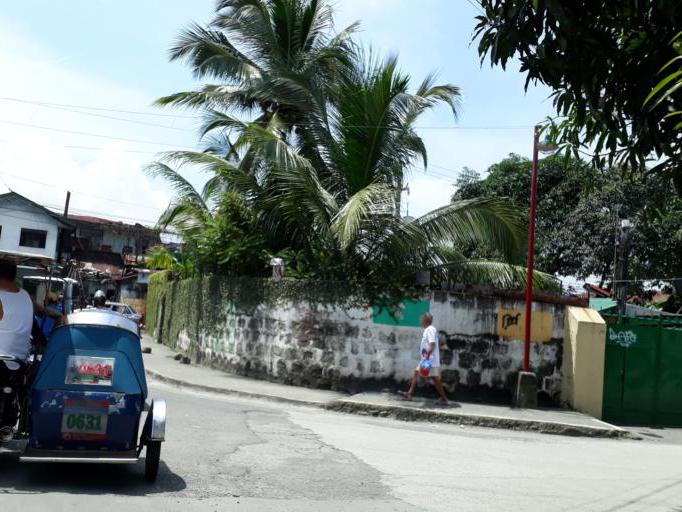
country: PH
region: Calabarzon
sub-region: Province of Rizal
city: Valenzuela
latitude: 14.6753
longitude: 120.9880
